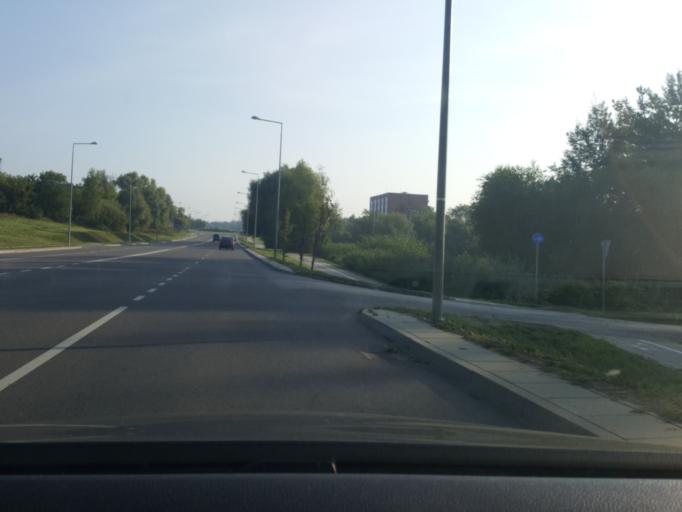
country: LT
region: Alytaus apskritis
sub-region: Alytus
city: Alytus
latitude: 54.4213
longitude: 24.0293
